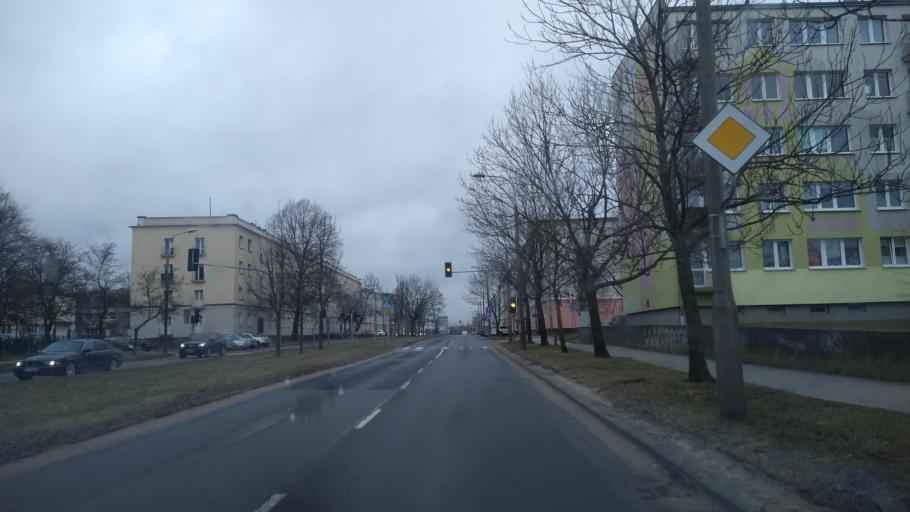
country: PL
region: Warmian-Masurian Voivodeship
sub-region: Powiat olsztynski
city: Olsztyn
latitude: 53.7763
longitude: 20.5027
